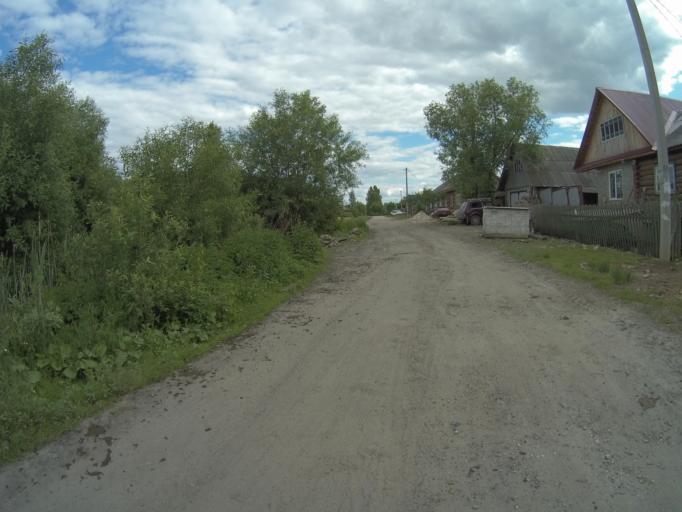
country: RU
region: Vladimir
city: Sudogda
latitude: 55.9554
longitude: 40.8447
